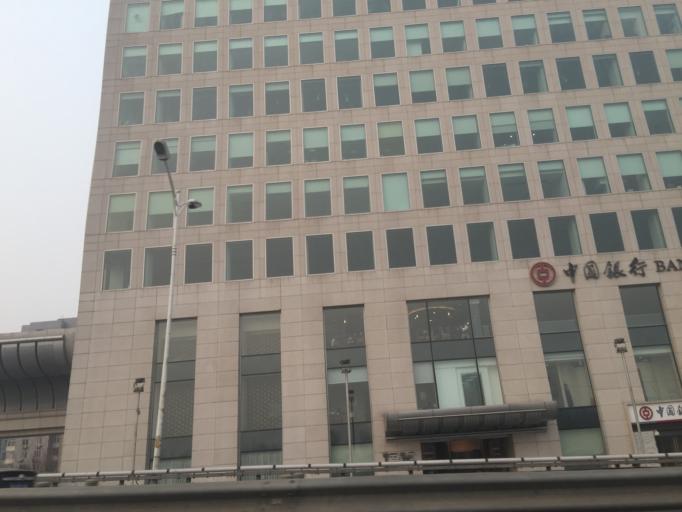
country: CN
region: Beijing
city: Datun
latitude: 39.9879
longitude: 116.3813
